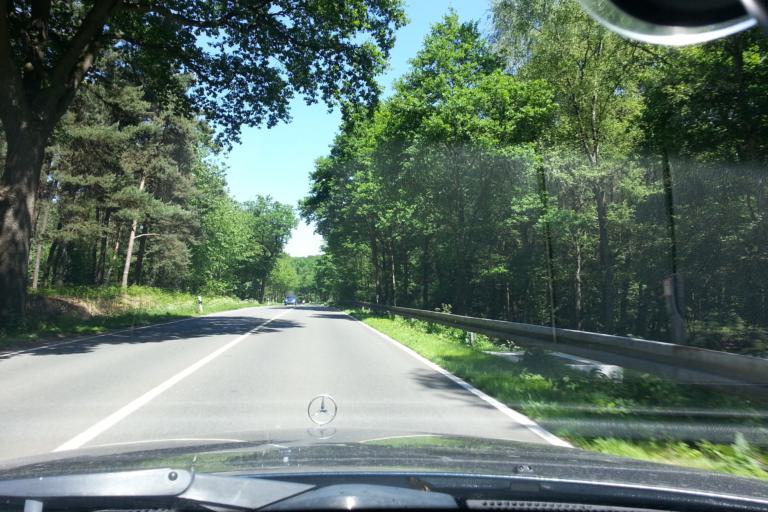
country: DE
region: North Rhine-Westphalia
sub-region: Regierungsbezirk Munster
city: Haltern
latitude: 51.7045
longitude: 7.1922
